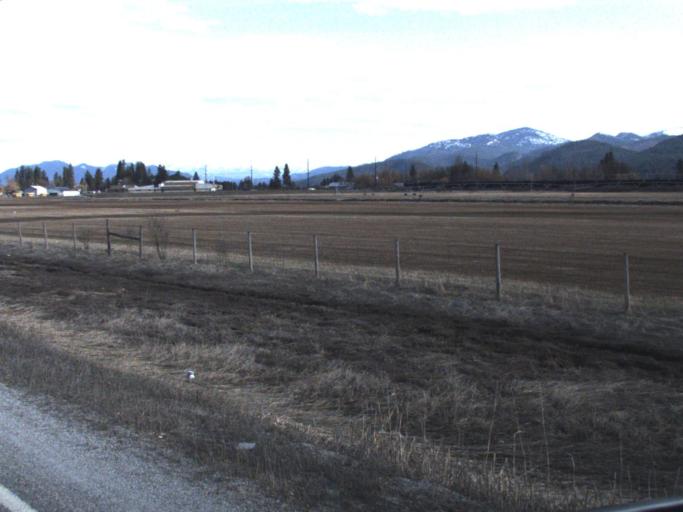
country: US
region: Washington
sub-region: Pend Oreille County
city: Newport
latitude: 48.3279
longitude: -117.2991
